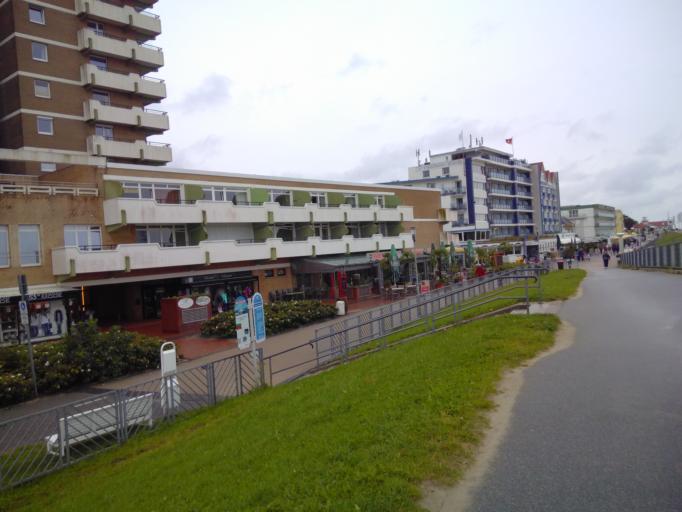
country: DE
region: Lower Saxony
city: Cuxhaven
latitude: 53.8862
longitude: 8.6415
